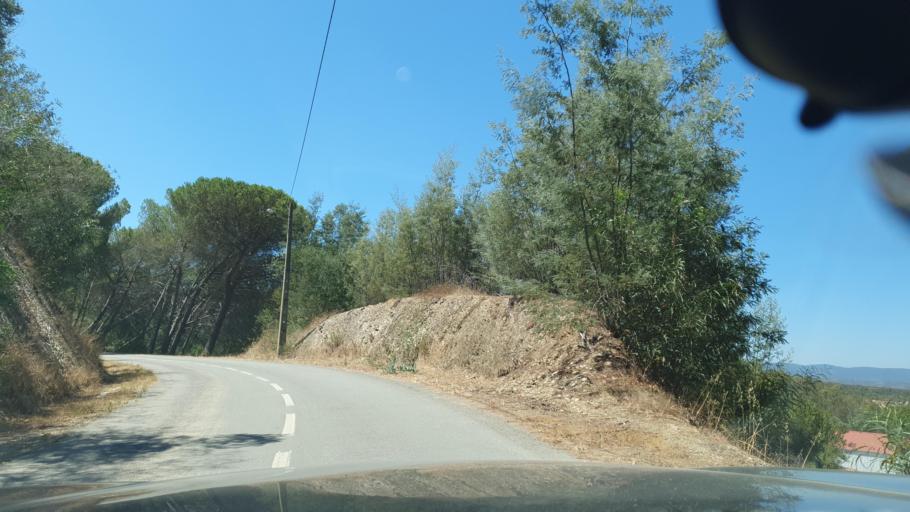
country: PT
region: Beja
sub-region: Odemira
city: Odemira
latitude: 37.5092
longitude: -8.4384
